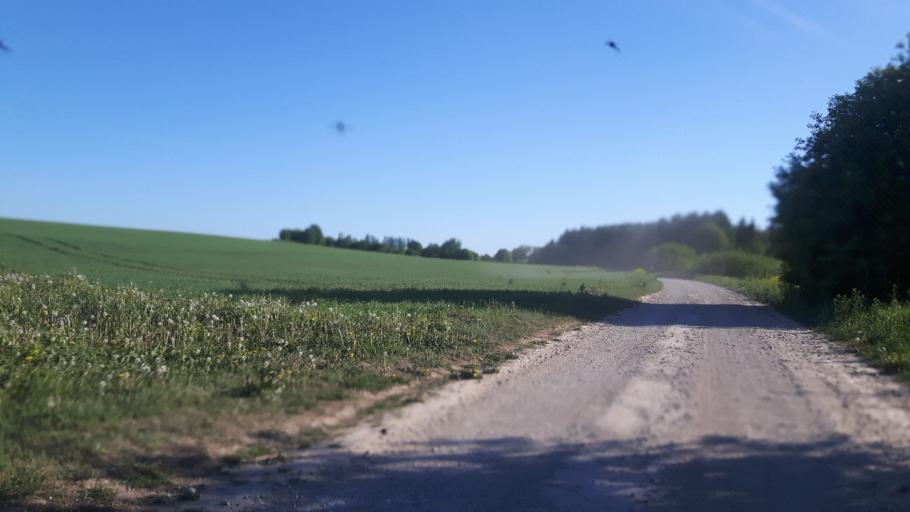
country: EE
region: Ida-Virumaa
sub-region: Puessi linn
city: Pussi
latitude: 59.4240
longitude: 27.0659
